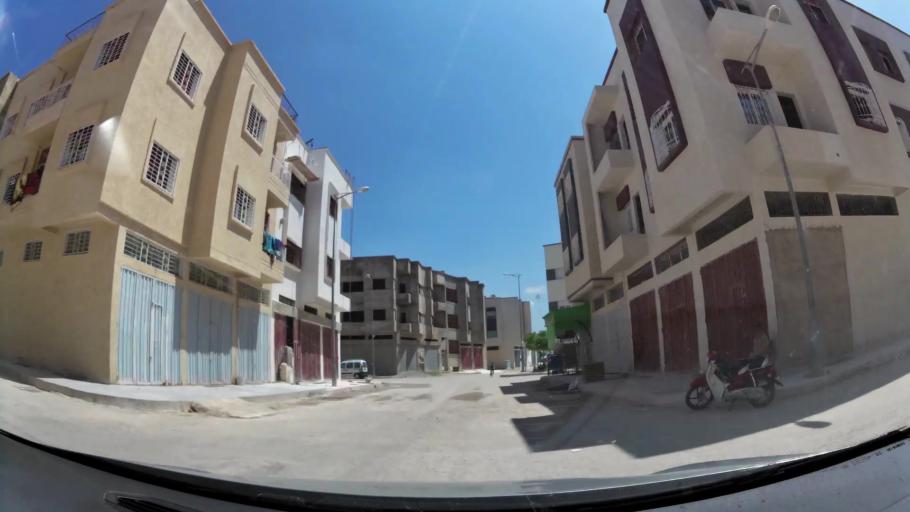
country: MA
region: Fes-Boulemane
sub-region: Fes
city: Fes
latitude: 34.0206
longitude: -5.0573
